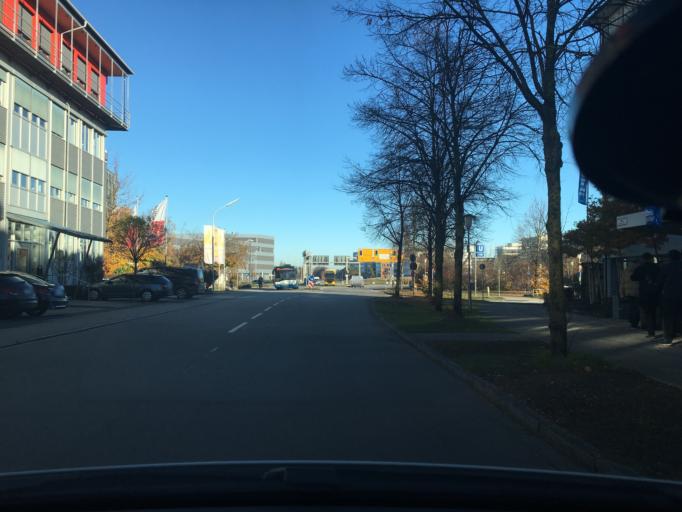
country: DE
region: Bavaria
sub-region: Upper Bavaria
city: Garching bei Munchen
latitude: 48.2480
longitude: 11.6302
